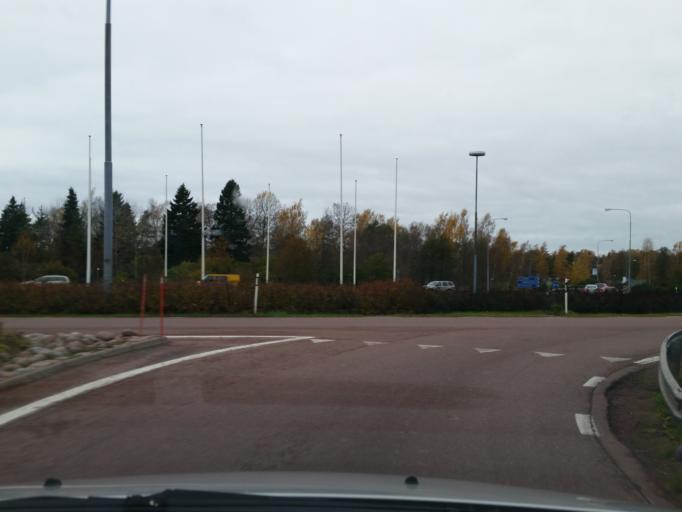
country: AX
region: Mariehamns stad
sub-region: Mariehamn
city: Mariehamn
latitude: 60.1137
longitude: 19.9303
